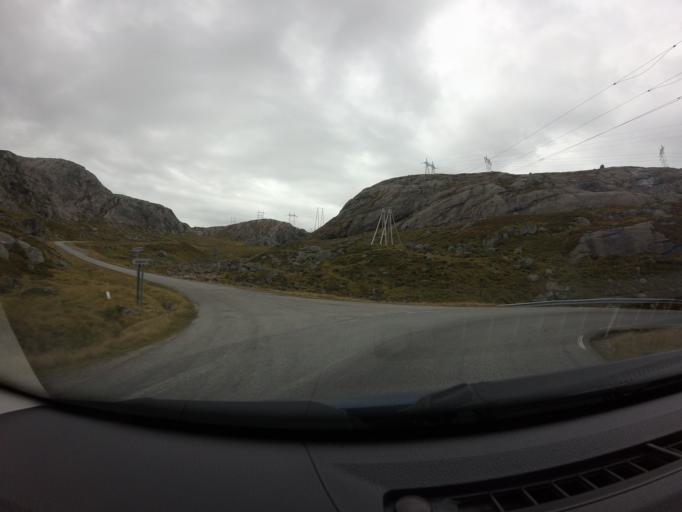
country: NO
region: Vest-Agder
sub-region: Sirdal
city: Tonstad
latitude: 59.0279
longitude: 6.6585
